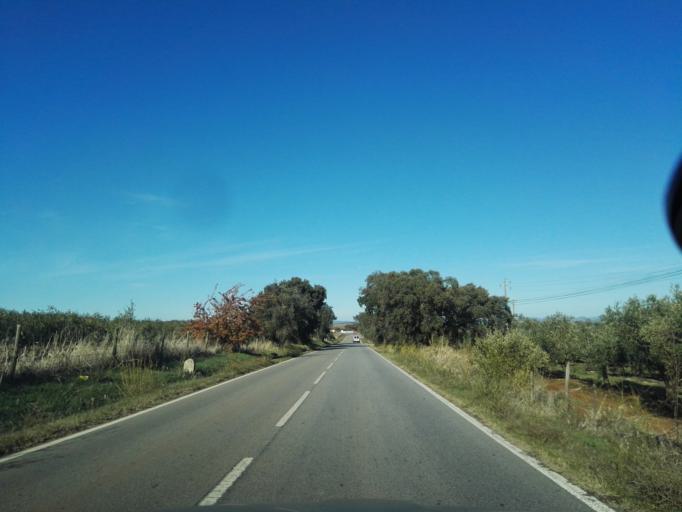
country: PT
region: Portalegre
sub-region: Elvas
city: Elvas
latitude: 38.9167
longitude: -7.1821
